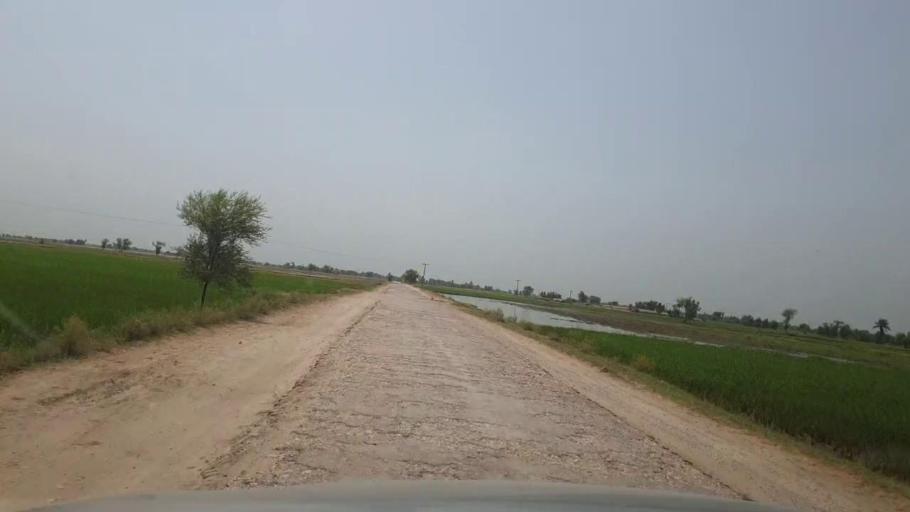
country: PK
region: Sindh
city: Garhi Yasin
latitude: 27.9182
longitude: 68.4040
